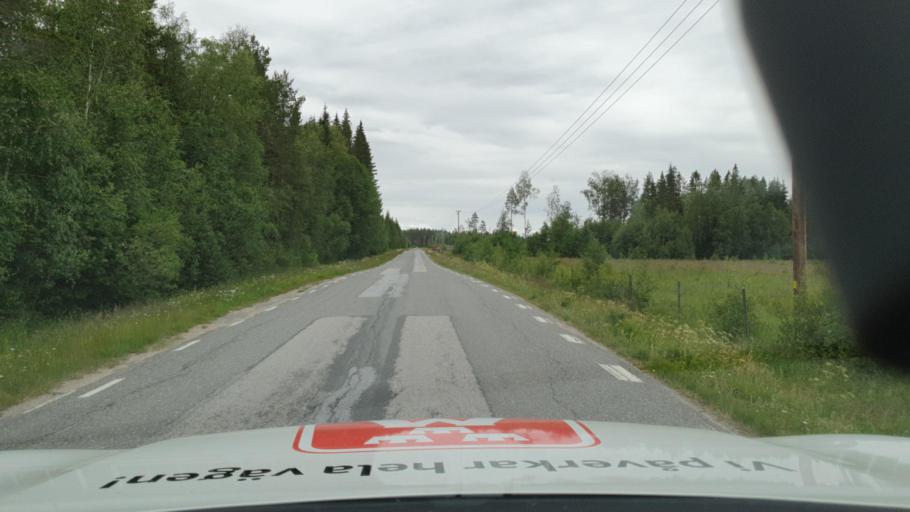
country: SE
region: Vaesterbotten
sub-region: Nordmalings Kommun
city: Nordmaling
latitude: 63.5112
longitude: 19.4212
